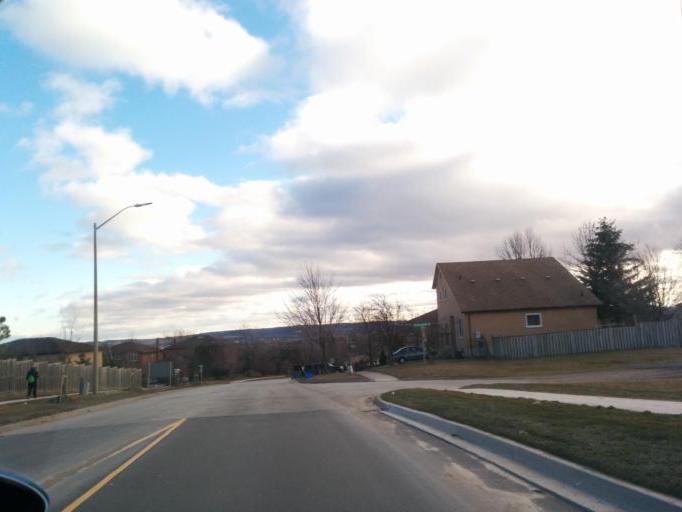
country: CA
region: Ontario
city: Bradford West Gwillimbury
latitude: 44.1057
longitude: -79.5781
